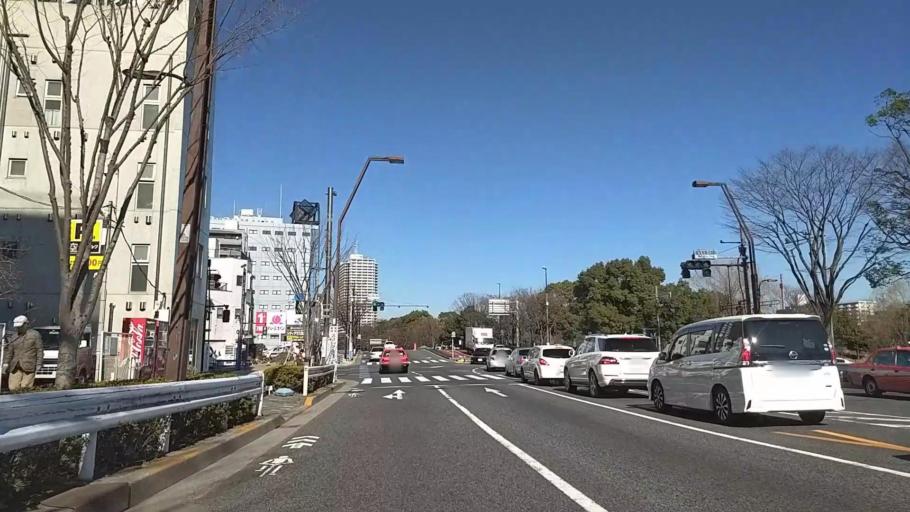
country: JP
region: Tokyo
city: Urayasu
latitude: 35.6749
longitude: 139.8068
